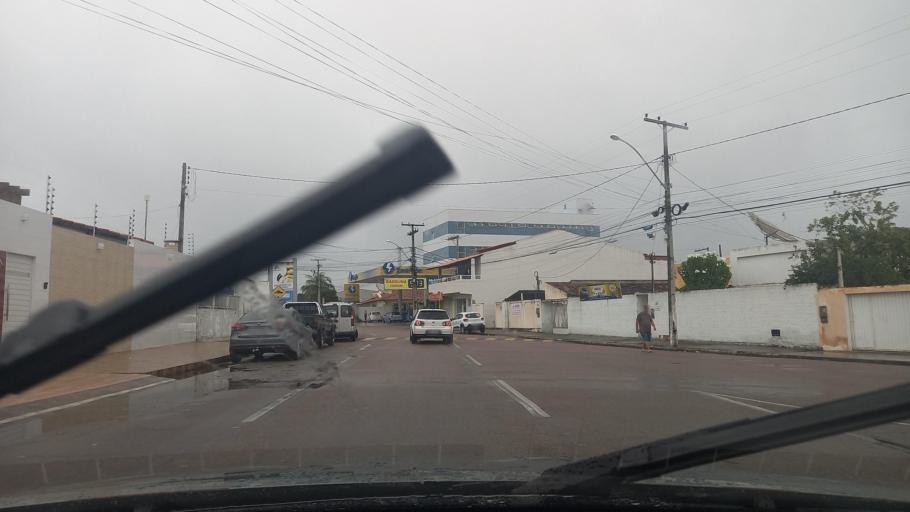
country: BR
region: Bahia
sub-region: Paulo Afonso
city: Paulo Afonso
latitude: -9.4065
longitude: -38.2246
